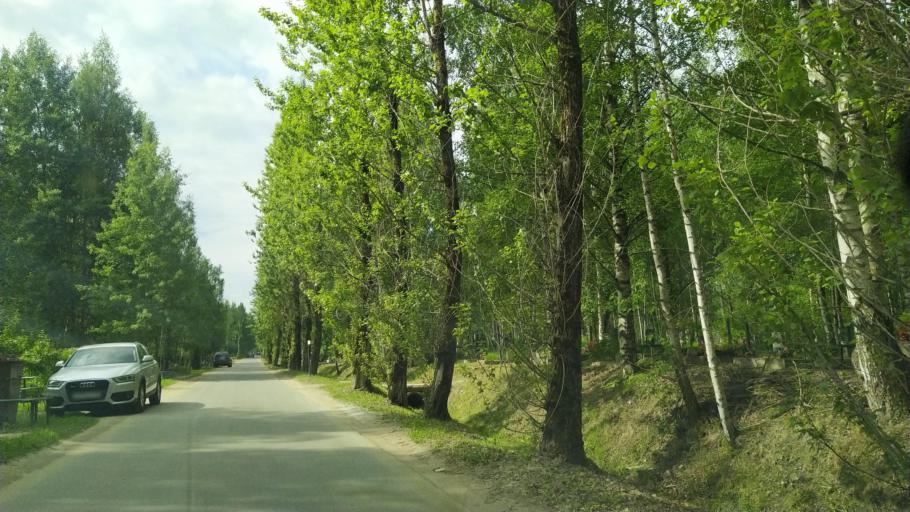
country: RU
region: St.-Petersburg
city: Dachnoye
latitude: 59.7693
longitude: 30.2643
